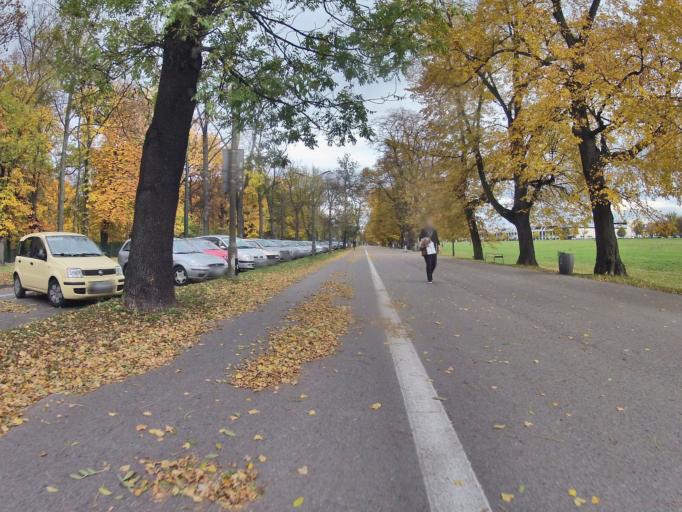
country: PL
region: Lesser Poland Voivodeship
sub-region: Krakow
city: Krakow
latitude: 50.0605
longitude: 19.9153
